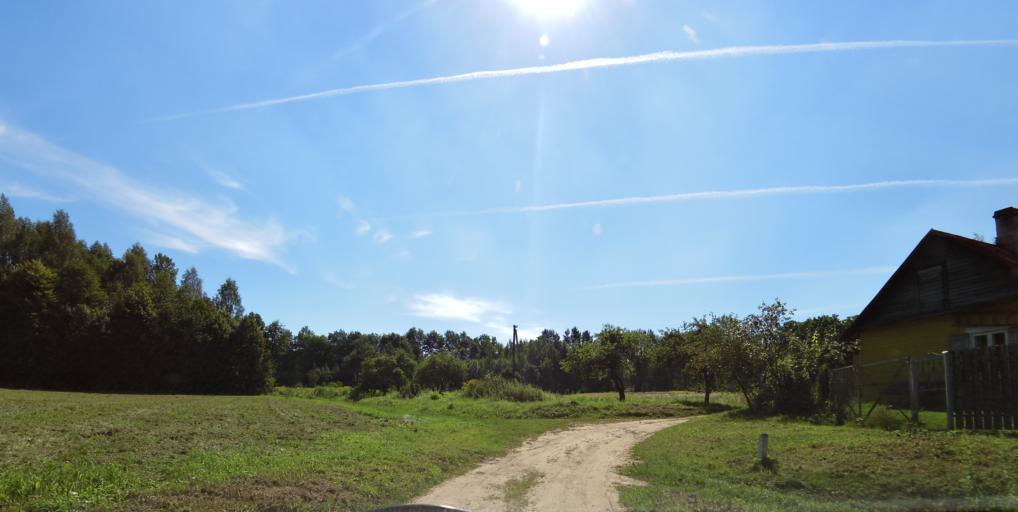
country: LT
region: Vilnius County
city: Rasos
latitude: 54.6837
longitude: 25.3635
